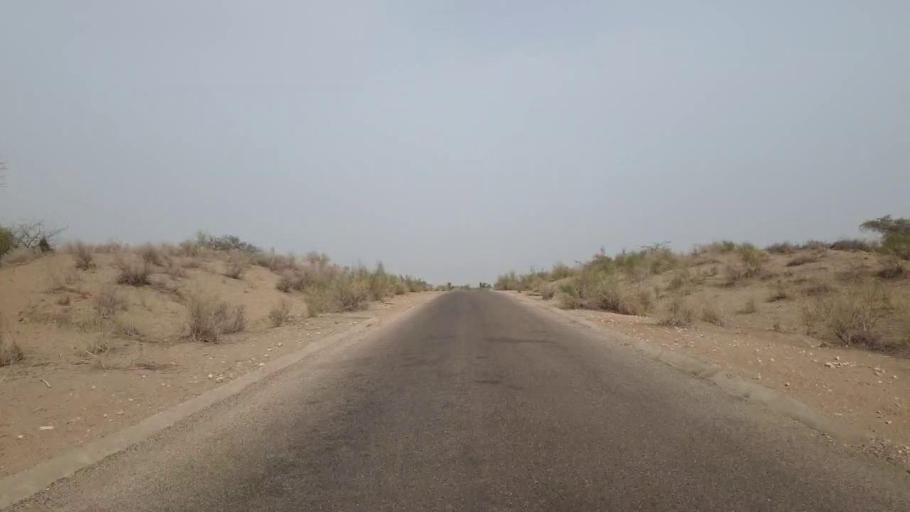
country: PK
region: Sindh
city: Islamkot
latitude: 24.5590
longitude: 70.3436
